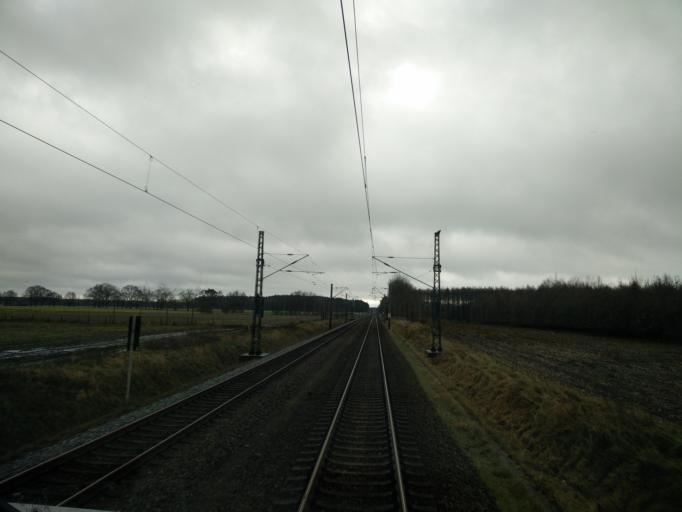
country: DE
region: Mecklenburg-Vorpommern
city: Rastow
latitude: 53.4044
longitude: 11.4679
